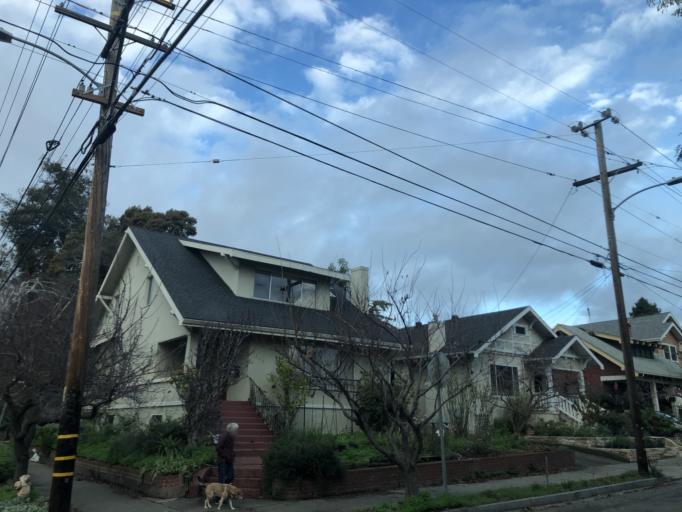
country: US
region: California
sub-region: Alameda County
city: Berkeley
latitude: 37.8468
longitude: -122.2564
